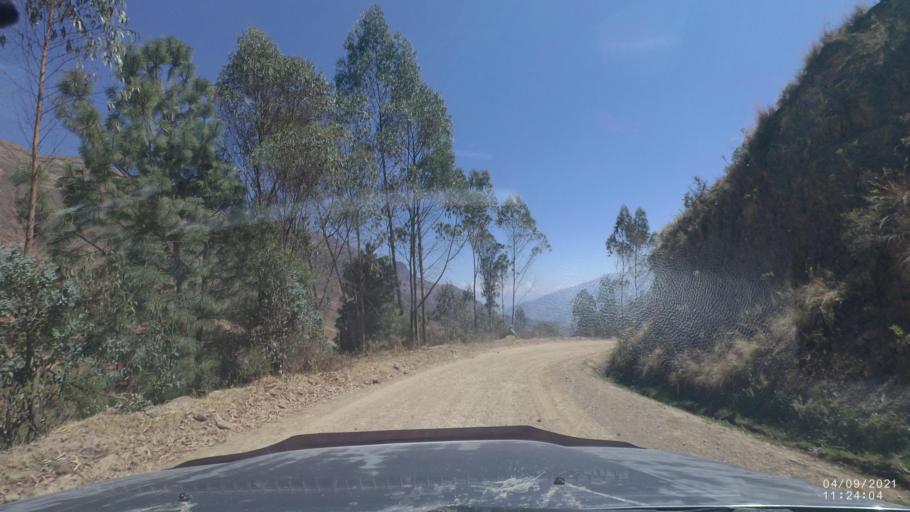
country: BO
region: Cochabamba
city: Colchani
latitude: -17.2607
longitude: -66.5088
